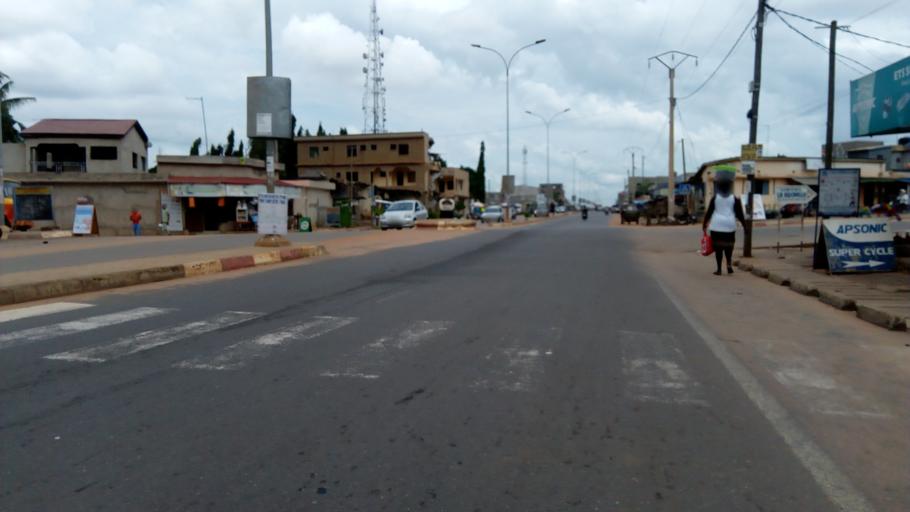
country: TG
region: Maritime
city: Lome
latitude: 6.2116
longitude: 1.1771
